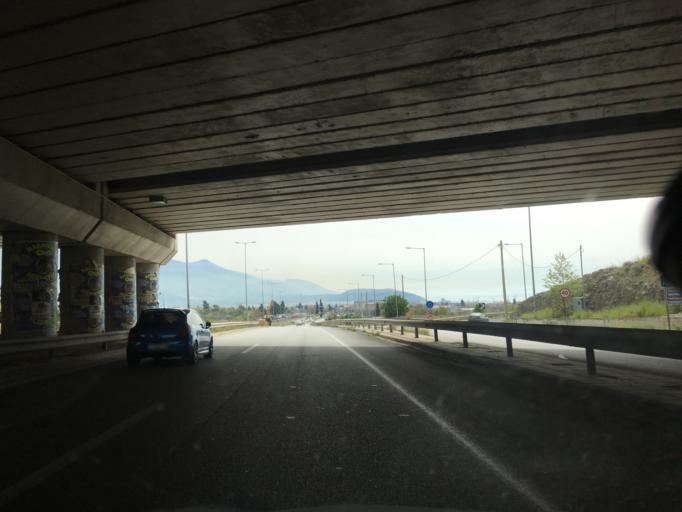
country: GR
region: Thessaly
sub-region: Nomos Magnisias
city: Nea Ionia
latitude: 39.3741
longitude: 22.9036
